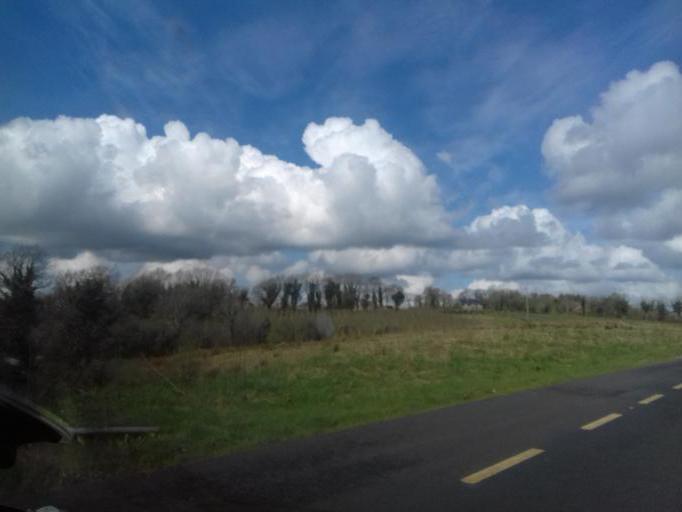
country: IE
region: Ulster
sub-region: An Cabhan
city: Belturbet
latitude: 54.0807
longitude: -7.4328
